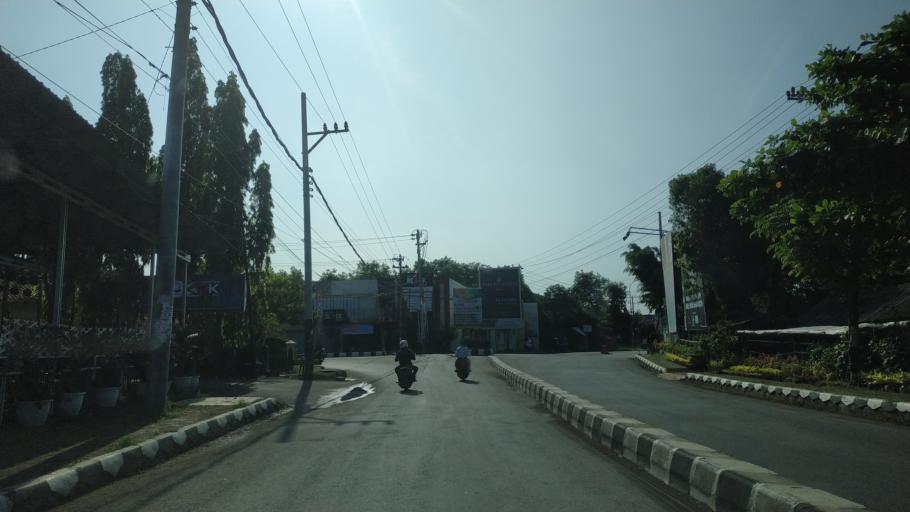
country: ID
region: Central Java
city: Pemalang
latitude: -6.9035
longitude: 109.3874
